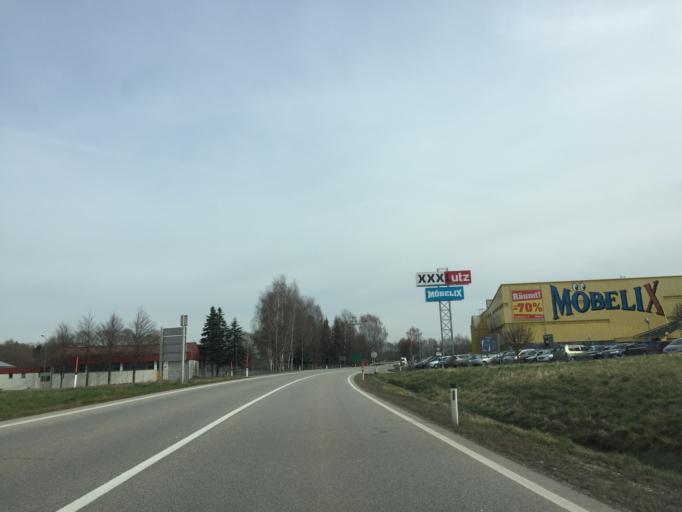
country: AT
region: Upper Austria
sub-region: Politischer Bezirk Ried im Innkreis
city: Ried im Innkreis
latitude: 48.2232
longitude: 13.4784
